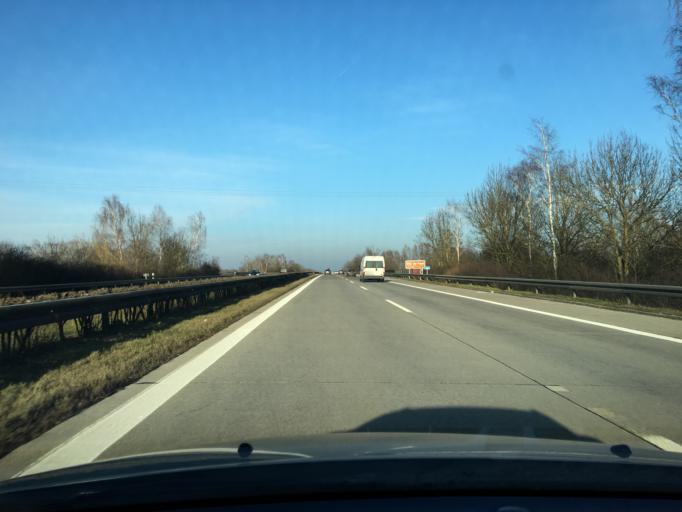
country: DE
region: Bavaria
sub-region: Upper Bavaria
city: Langenpreising
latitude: 48.4604
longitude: 11.9751
